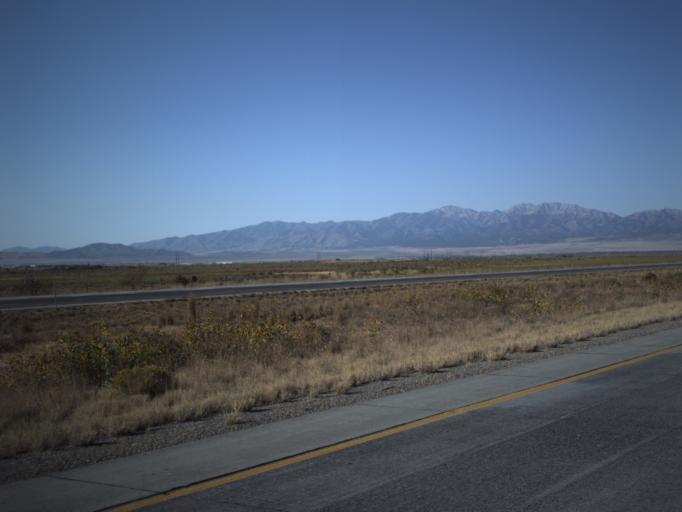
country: US
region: Utah
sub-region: Tooele County
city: Stansbury park
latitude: 40.6639
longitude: -112.3223
